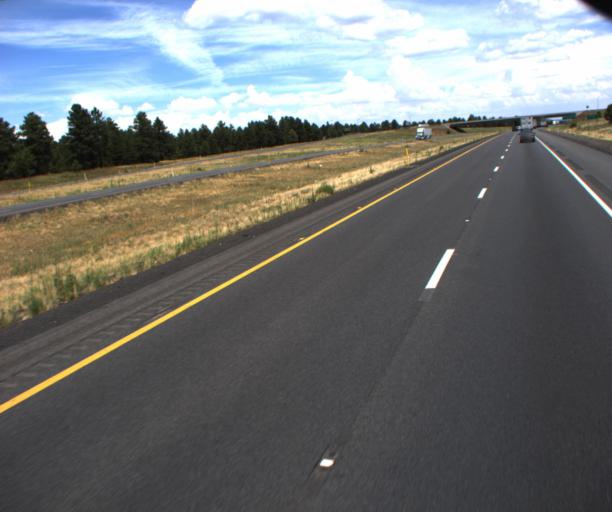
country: US
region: Arizona
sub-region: Coconino County
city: Williams
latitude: 35.2418
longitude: -112.2170
